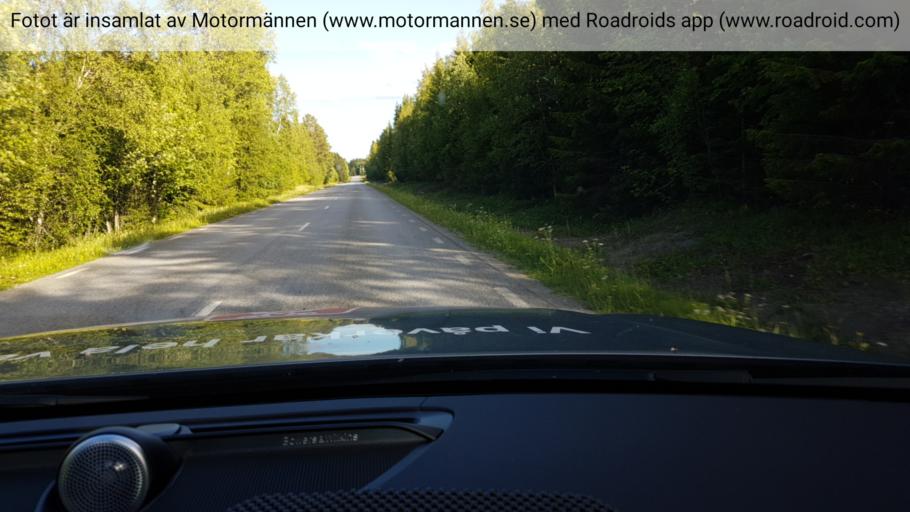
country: SE
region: Jaemtland
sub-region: Krokoms Kommun
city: Krokom
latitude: 63.1569
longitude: 14.1420
